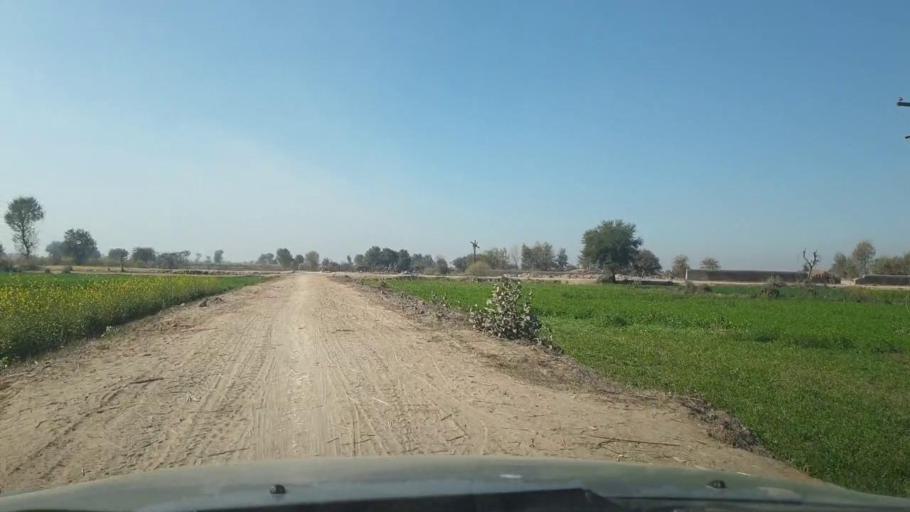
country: PK
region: Sindh
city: Ghotki
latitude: 28.0335
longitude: 69.2475
